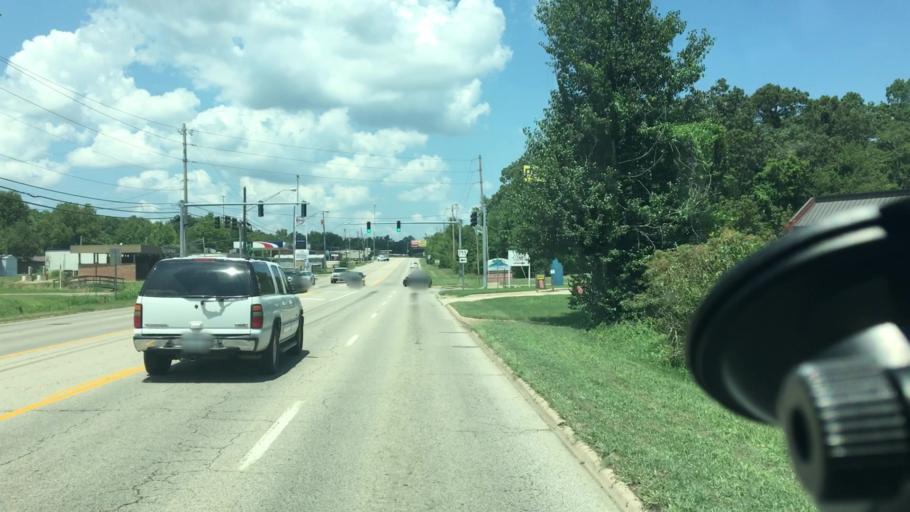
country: US
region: Arkansas
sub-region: Sebastian County
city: Barling
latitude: 35.3349
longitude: -94.3135
